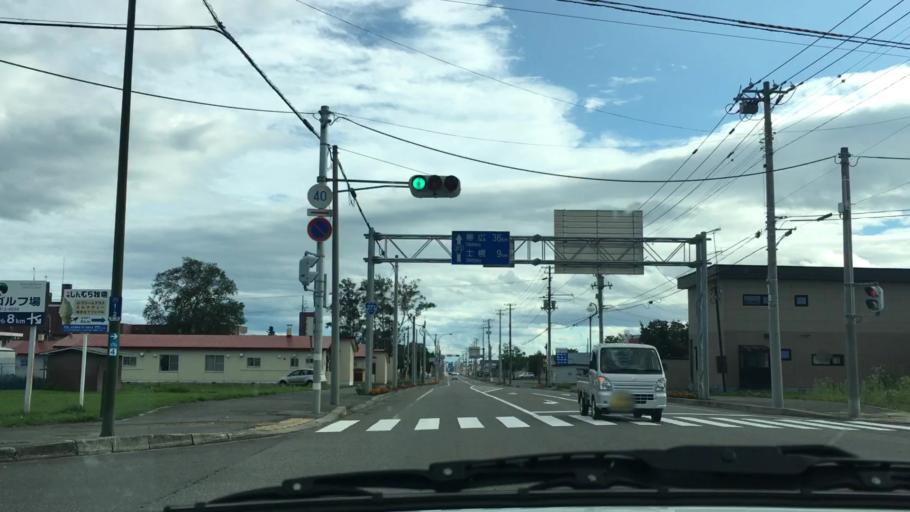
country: JP
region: Hokkaido
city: Otofuke
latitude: 43.2347
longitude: 143.2955
